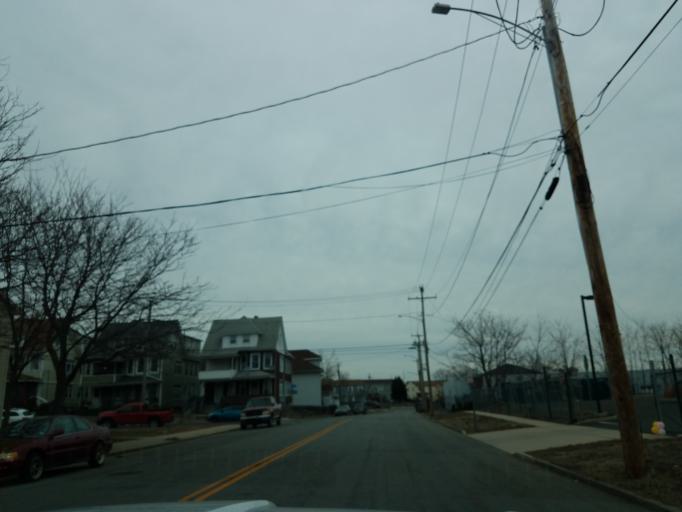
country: US
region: Connecticut
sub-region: Fairfield County
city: Bridgeport
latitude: 41.1797
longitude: -73.1764
